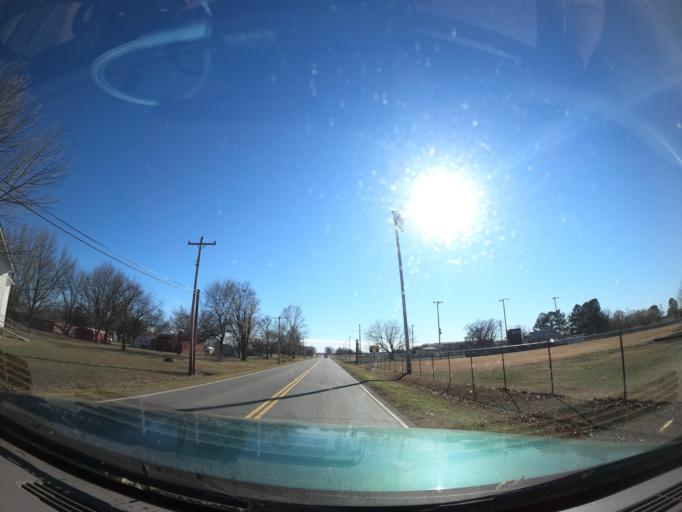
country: US
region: Oklahoma
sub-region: McIntosh County
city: Checotah
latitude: 35.5544
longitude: -95.6515
